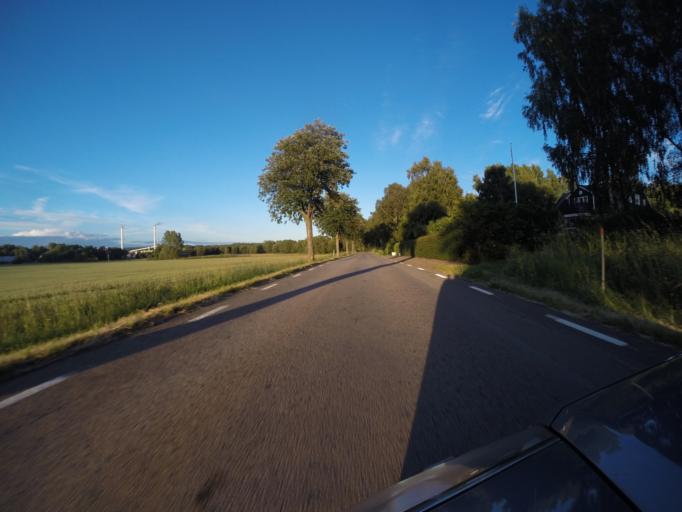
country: SE
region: Skane
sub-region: Bjuvs Kommun
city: Billesholm
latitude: 56.0490
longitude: 12.9567
